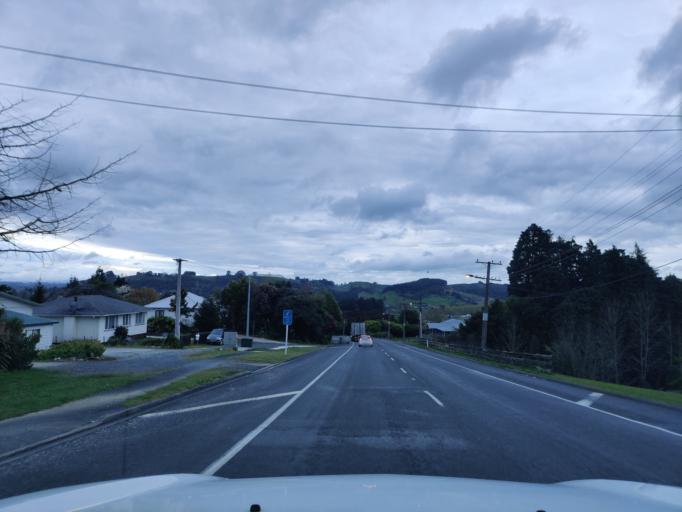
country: NZ
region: Waikato
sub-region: Otorohanga District
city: Otorohanga
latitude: -38.3472
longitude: 175.1678
